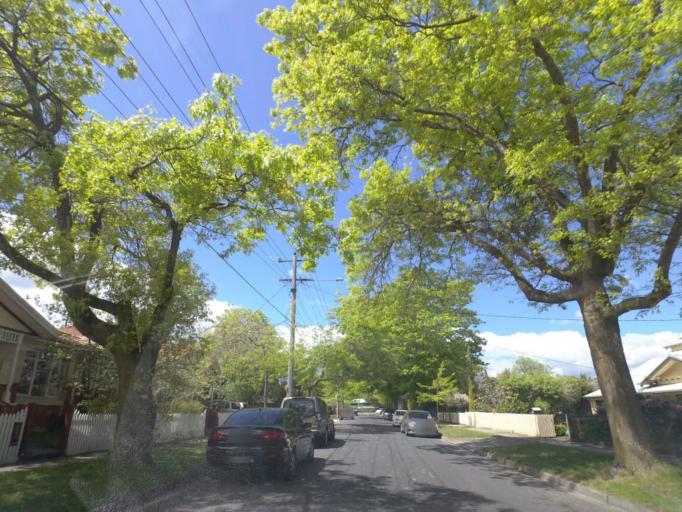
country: AU
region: Victoria
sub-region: Whitehorse
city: Box Hill
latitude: -37.8153
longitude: 145.1382
